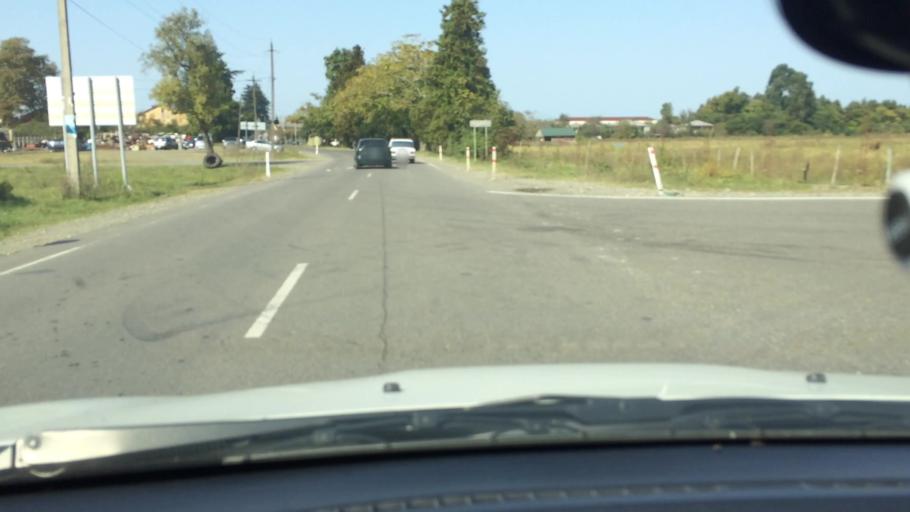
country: GE
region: Ajaria
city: Kobuleti
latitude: 41.8068
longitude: 41.7933
